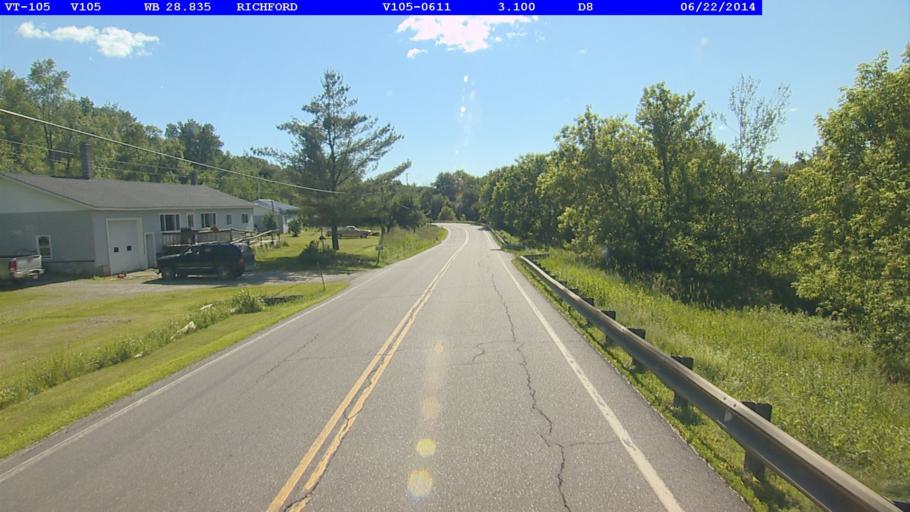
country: US
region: Vermont
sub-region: Franklin County
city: Richford
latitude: 44.9865
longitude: -72.6564
